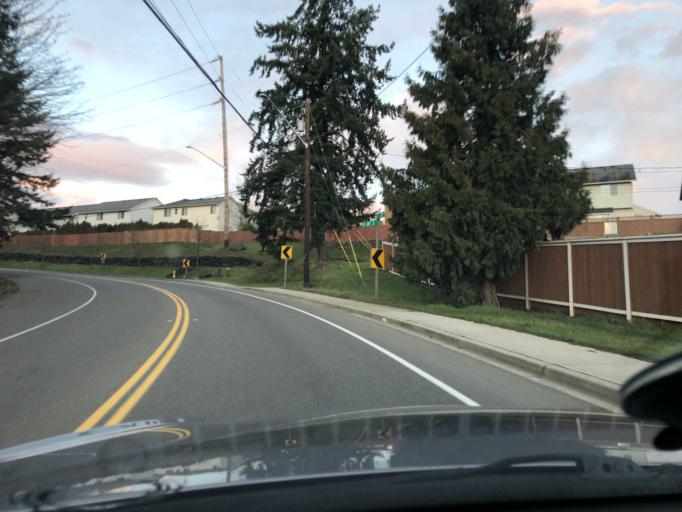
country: US
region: Washington
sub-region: King County
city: Lakeland North
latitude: 47.3146
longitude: -122.2715
